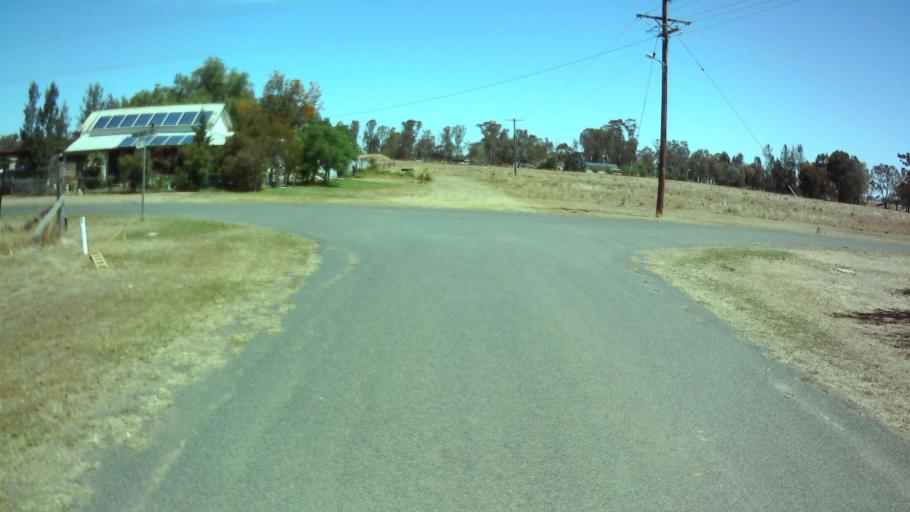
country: AU
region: New South Wales
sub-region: Weddin
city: Grenfell
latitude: -34.0127
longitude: 147.7914
